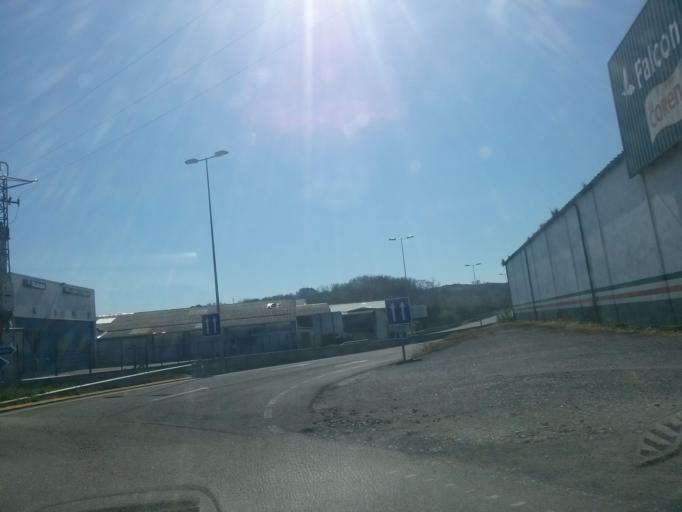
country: ES
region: Galicia
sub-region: Provincia de Lugo
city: Lugo
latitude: 43.0314
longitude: -7.5357
